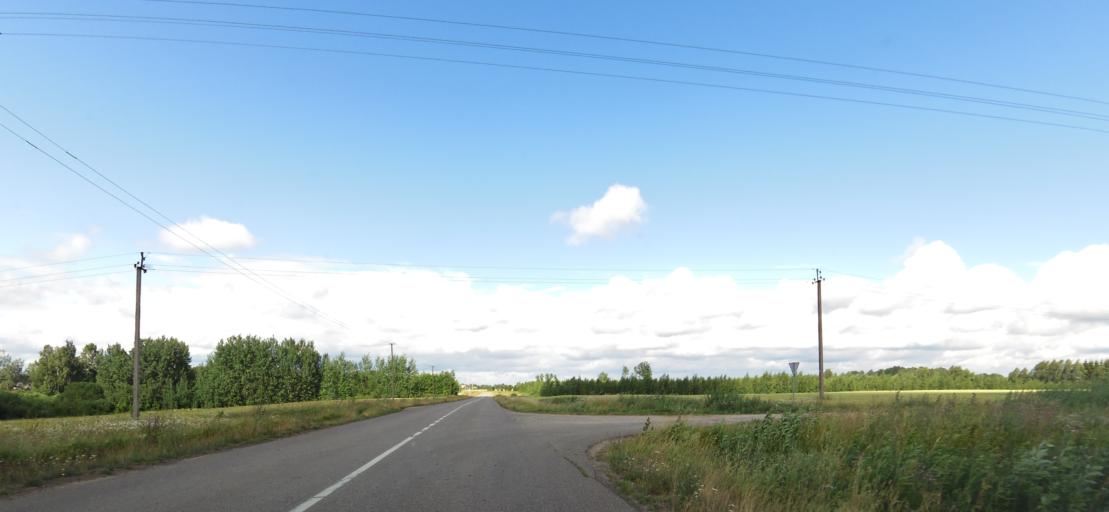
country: LT
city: Kupiskis
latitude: 55.9050
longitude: 25.0315
